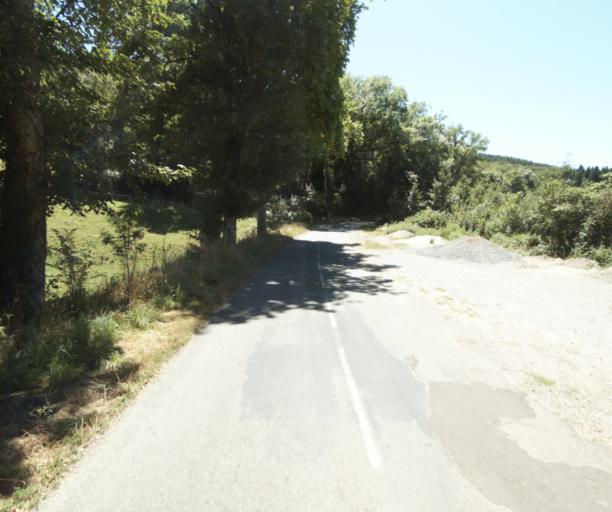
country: FR
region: Midi-Pyrenees
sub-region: Departement du Tarn
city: Dourgne
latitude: 43.4260
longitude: 2.1709
